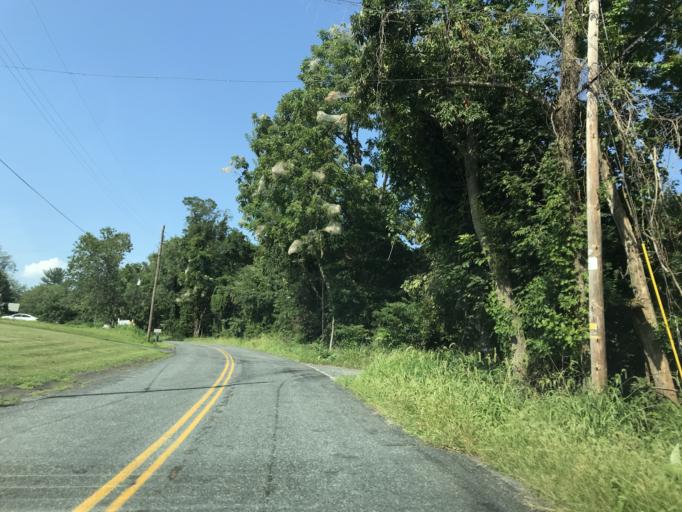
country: US
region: Maryland
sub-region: Harford County
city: South Bel Air
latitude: 39.6216
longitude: -76.2785
